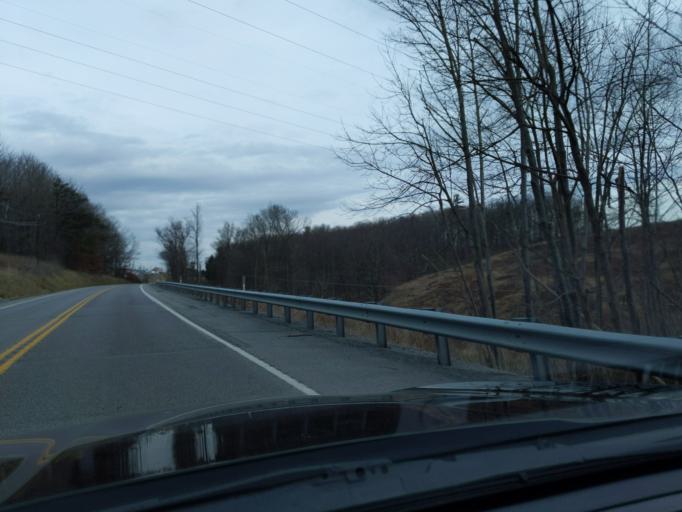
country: US
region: Pennsylvania
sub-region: Blair County
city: Lakemont
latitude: 40.4611
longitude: -78.3185
